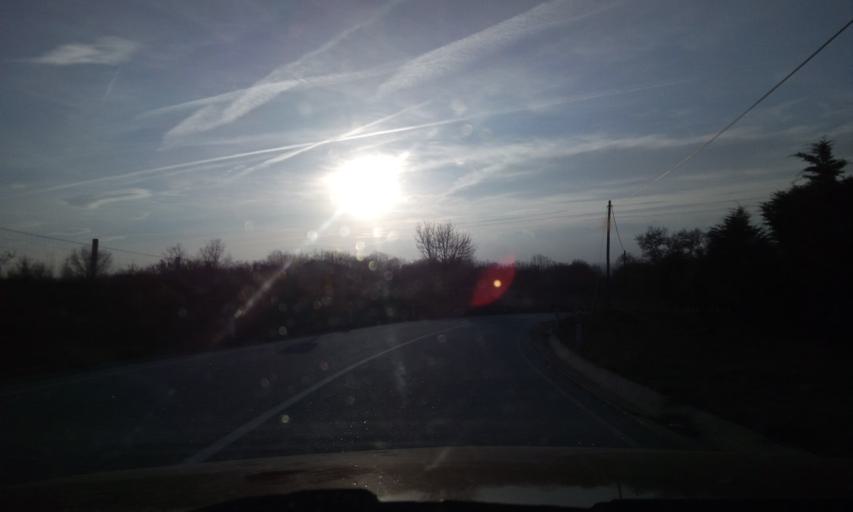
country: PT
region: Guarda
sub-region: Pinhel
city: Pinhel
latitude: 40.6028
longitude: -7.0152
